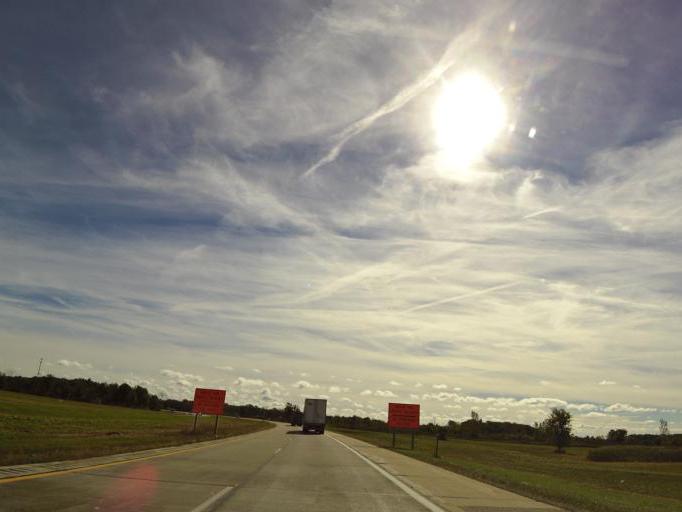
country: US
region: Michigan
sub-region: Saint Clair County
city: Capac
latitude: 42.9789
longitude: -82.8414
